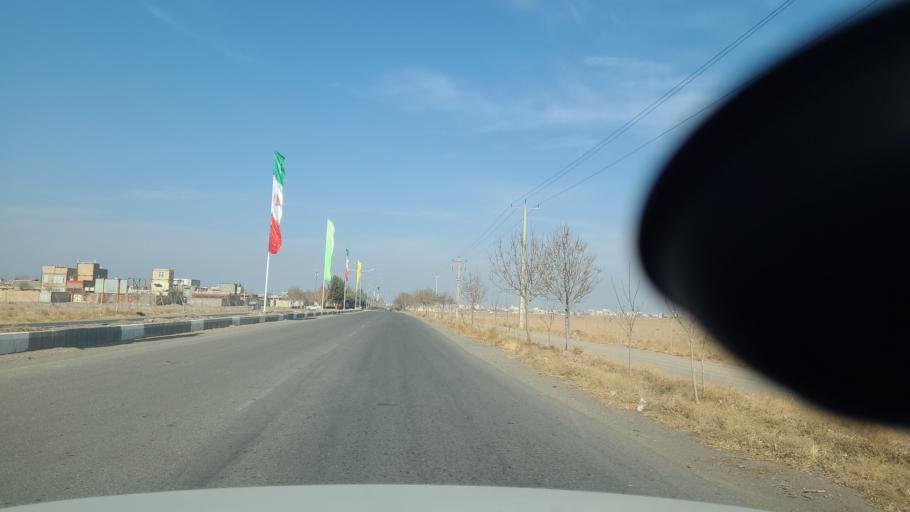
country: IR
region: Razavi Khorasan
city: Fariman
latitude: 35.6795
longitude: 59.8430
